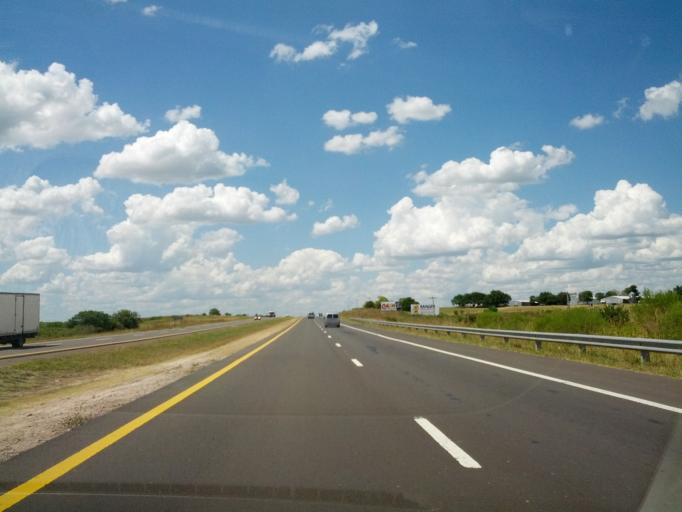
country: AR
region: Entre Rios
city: Colonia Elia
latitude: -32.5632
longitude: -58.3707
